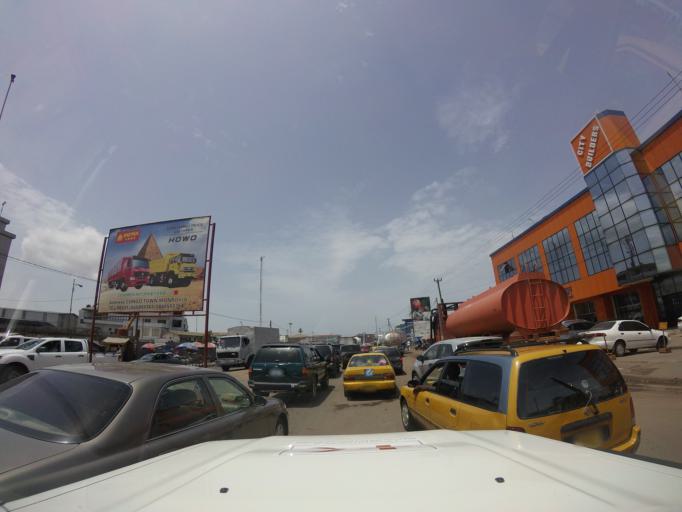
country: LR
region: Montserrado
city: Monrovia
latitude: 6.3360
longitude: -10.7947
